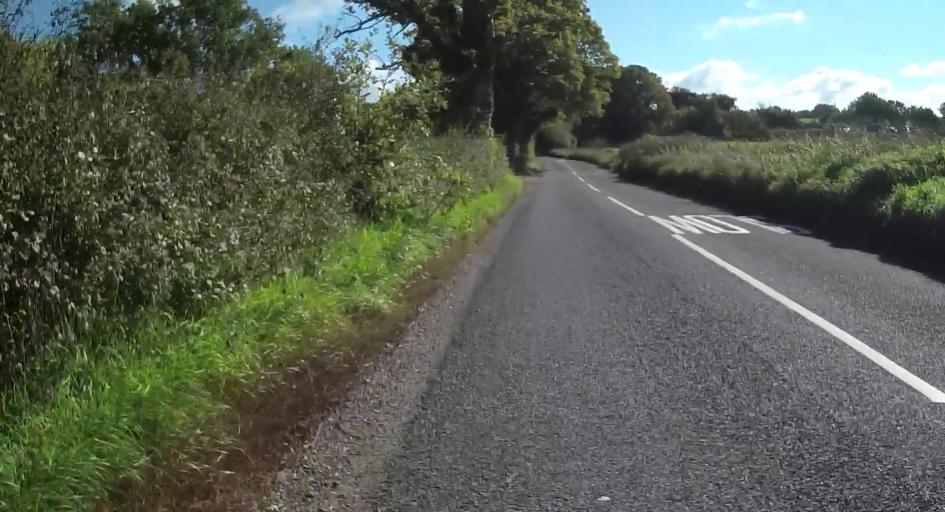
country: GB
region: England
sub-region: Hampshire
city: Old Basing
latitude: 51.2647
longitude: -1.0083
